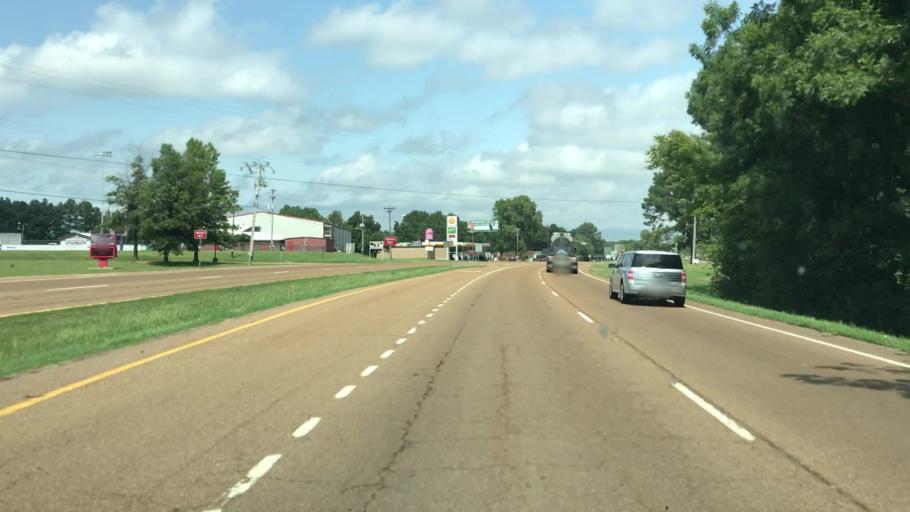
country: US
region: Tennessee
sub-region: Obion County
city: Troy
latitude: 36.3428
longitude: -89.1539
